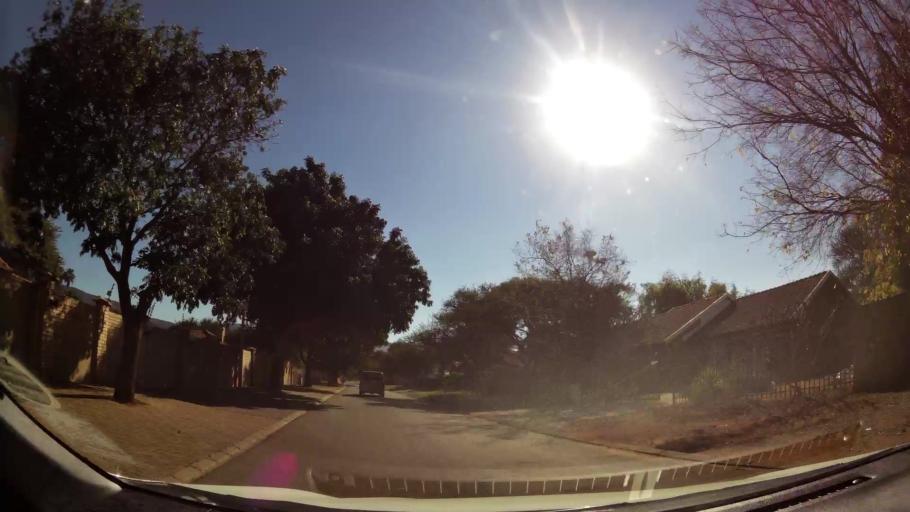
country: ZA
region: Limpopo
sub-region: Waterberg District Municipality
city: Mokopane
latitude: -24.2088
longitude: 28.9955
